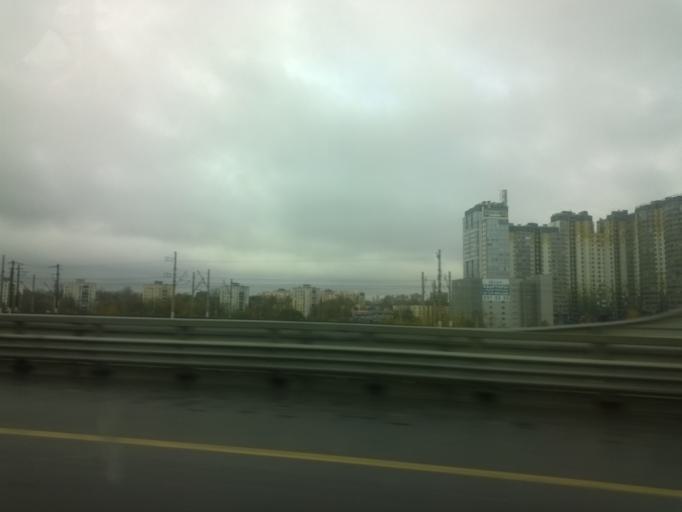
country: RU
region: St.-Petersburg
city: Avtovo
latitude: 59.8477
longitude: 30.2878
